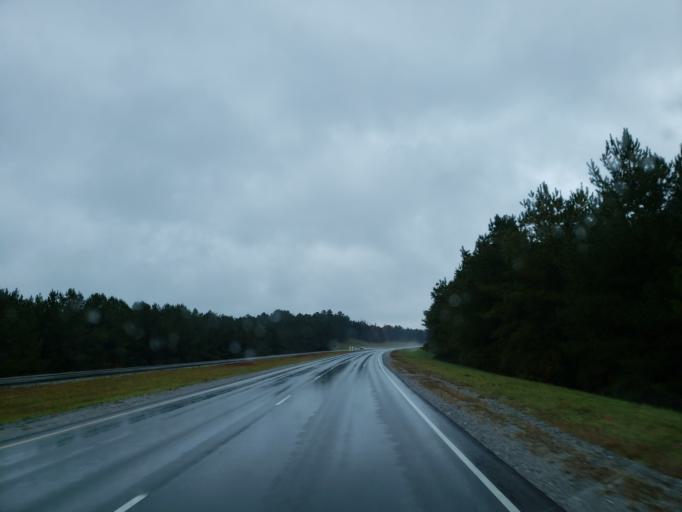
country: US
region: Mississippi
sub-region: Clarke County
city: Stonewall
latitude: 32.1975
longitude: -88.7073
